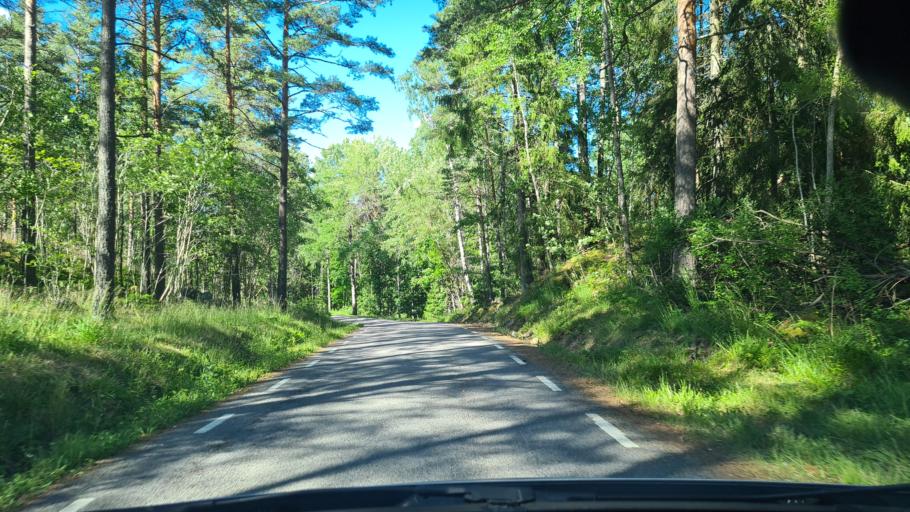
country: SE
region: OEstergoetland
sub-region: Norrkopings Kommun
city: Krokek
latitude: 58.7194
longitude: 16.4305
